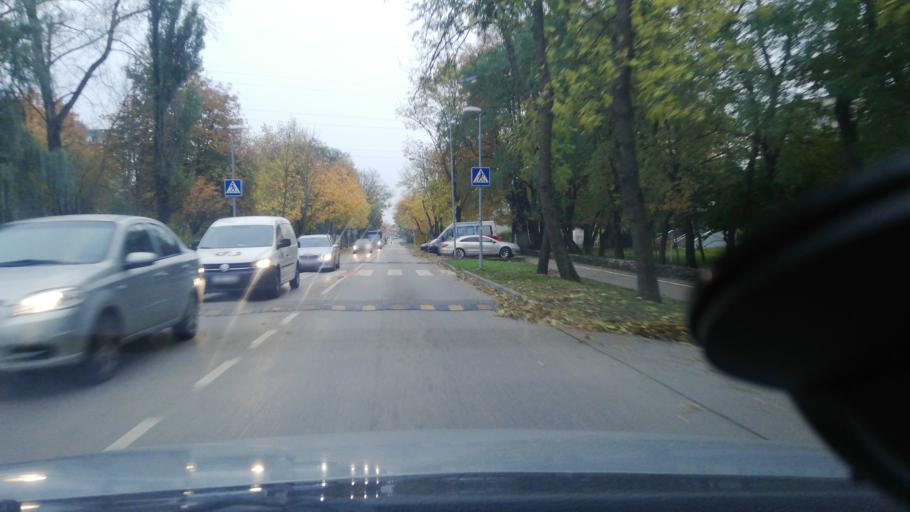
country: LT
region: Klaipedos apskritis
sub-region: Klaipeda
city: Klaipeda
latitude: 55.7274
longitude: 21.1317
